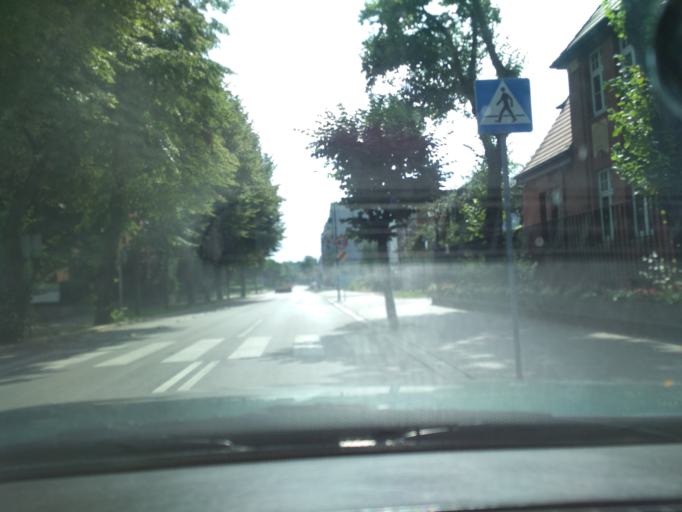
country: PL
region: Silesian Voivodeship
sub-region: Powiat raciborski
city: Raciborz
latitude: 50.0890
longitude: 18.2154
